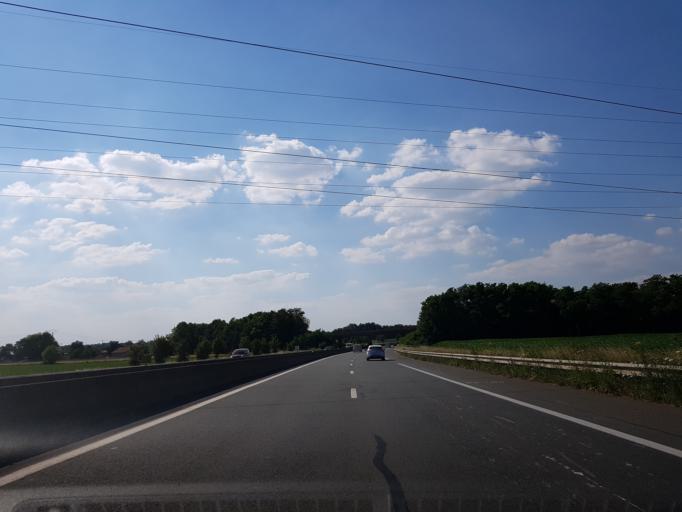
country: FR
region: Nord-Pas-de-Calais
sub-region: Departement du Nord
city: Escaudain
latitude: 50.3324
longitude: 3.3261
